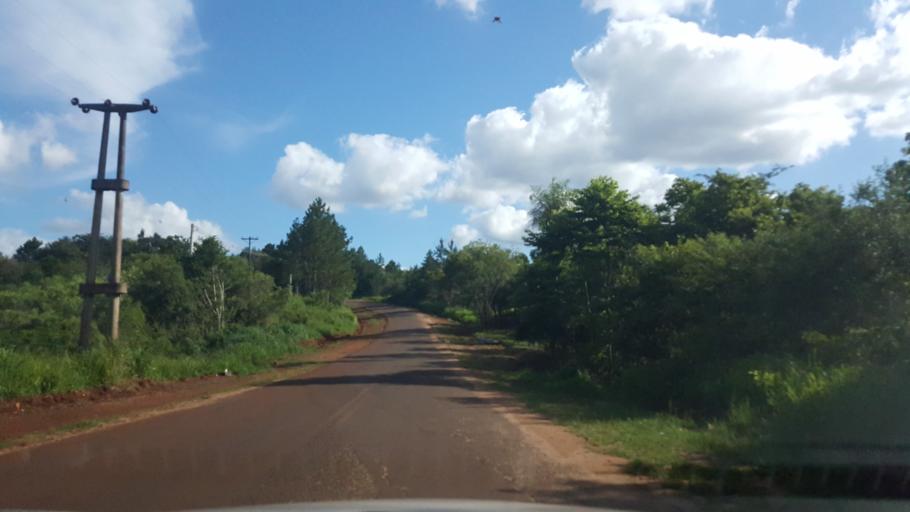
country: AR
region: Misiones
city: Santa Ana
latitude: -27.3596
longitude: -55.5873
